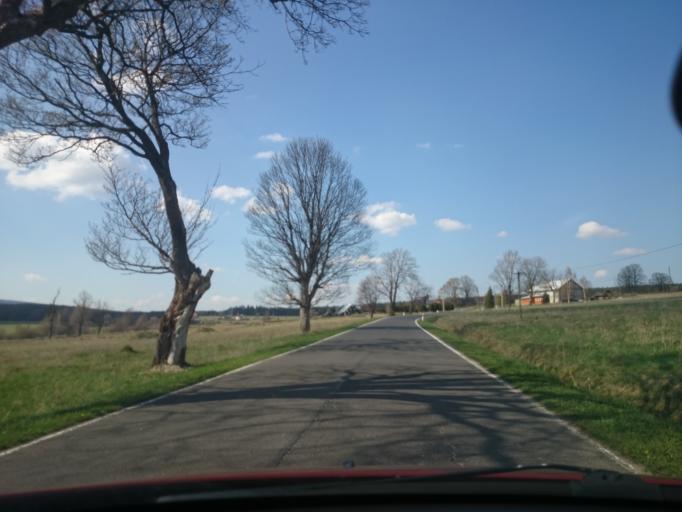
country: PL
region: Lower Silesian Voivodeship
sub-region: Powiat klodzki
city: Szczytna
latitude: 50.3064
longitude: 16.4506
